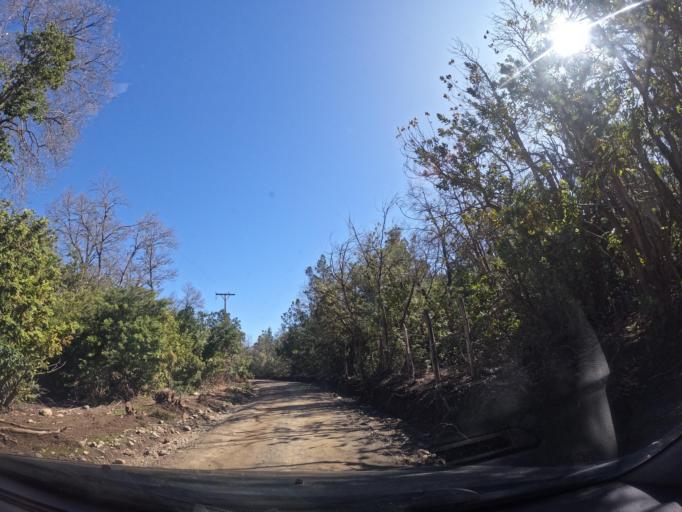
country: CL
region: Maule
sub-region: Provincia de Linares
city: Longavi
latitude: -36.2450
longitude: -71.3421
